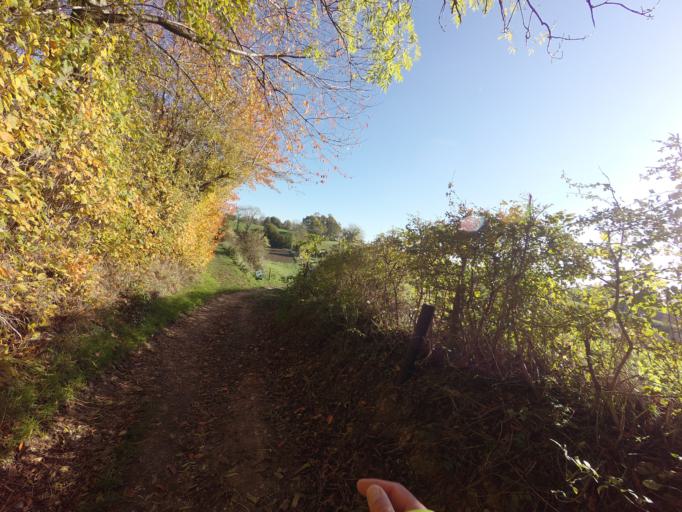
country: NL
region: Limburg
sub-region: Gemeente Voerendaal
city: Ubachsberg
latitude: 50.8403
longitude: 5.9412
